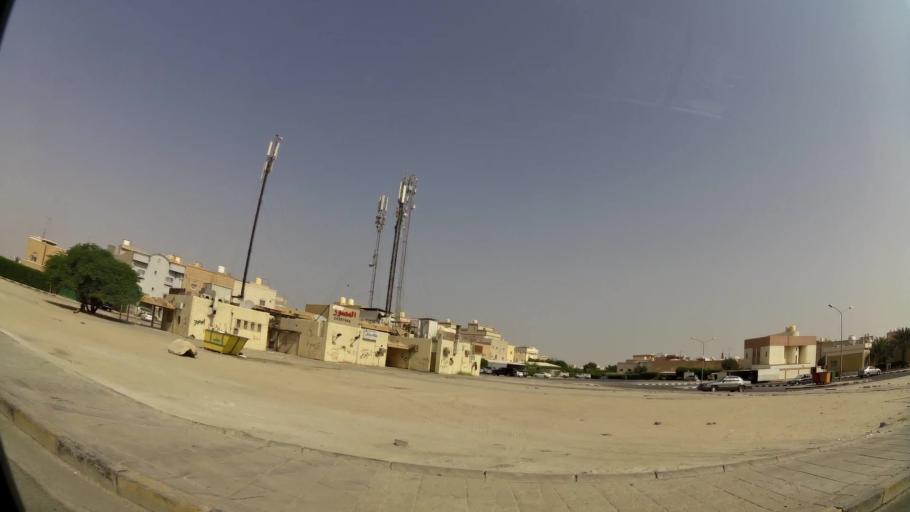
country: KW
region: Muhafazat al Jahra'
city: Al Jahra'
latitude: 29.3271
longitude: 47.6502
